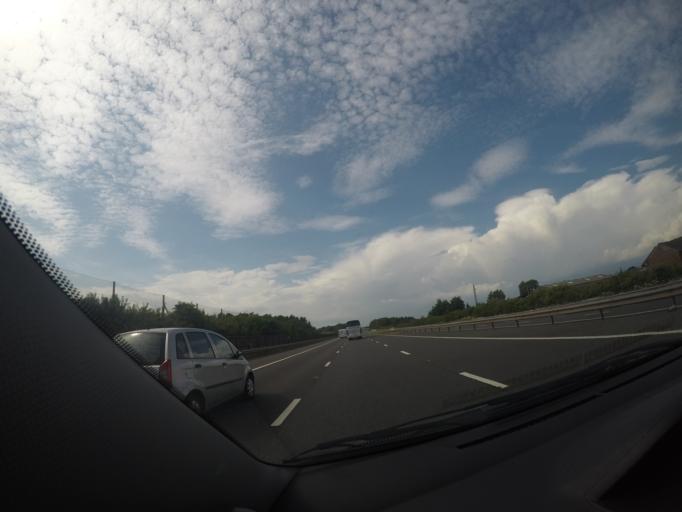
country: GB
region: Scotland
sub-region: Dumfries and Galloway
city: Gretna
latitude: 54.9638
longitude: -2.9957
